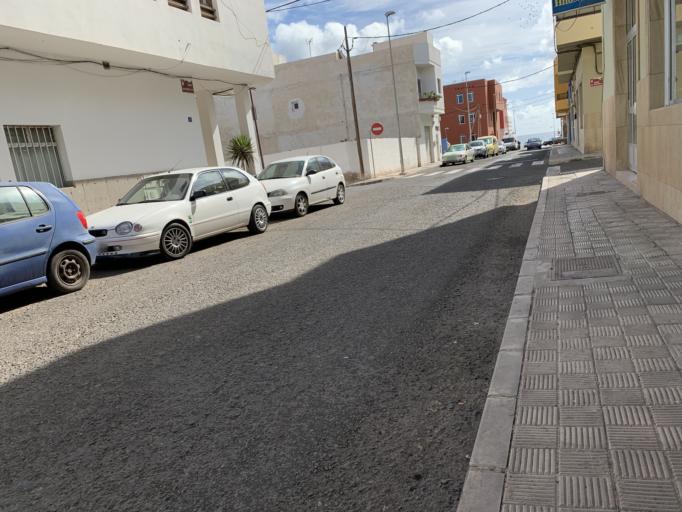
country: ES
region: Canary Islands
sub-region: Provincia de Las Palmas
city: Puerto del Rosario
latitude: 28.5031
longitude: -13.8489
